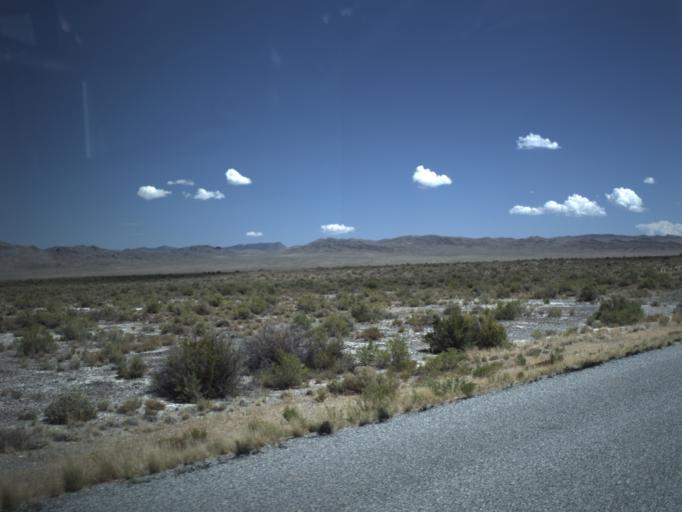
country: US
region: Nevada
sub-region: White Pine County
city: McGill
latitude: 39.0512
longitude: -113.9719
